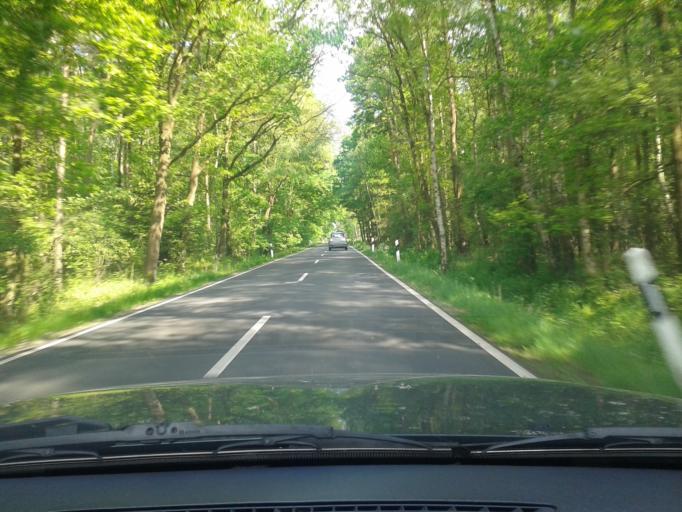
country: DE
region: Lower Saxony
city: Adelheidsdorf
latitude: 52.5219
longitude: 10.0528
